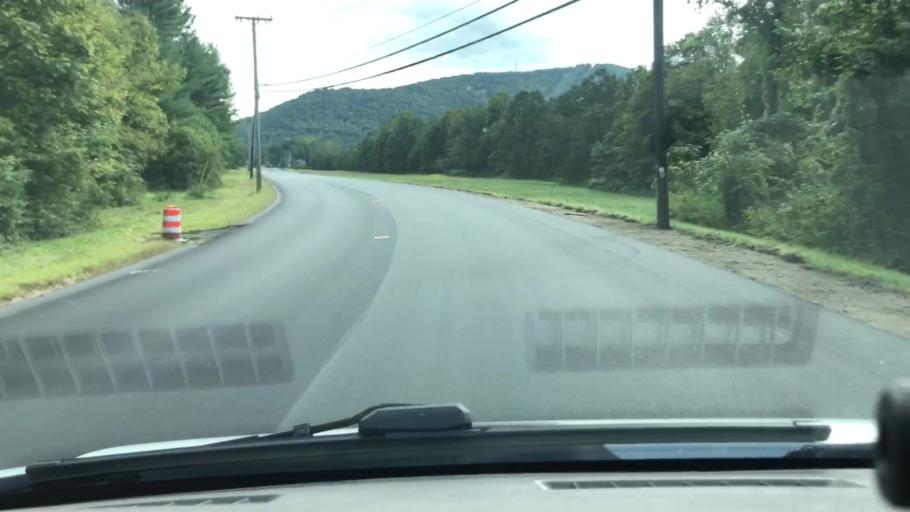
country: US
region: Massachusetts
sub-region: Franklin County
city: Charlemont
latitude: 42.6301
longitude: -72.8936
